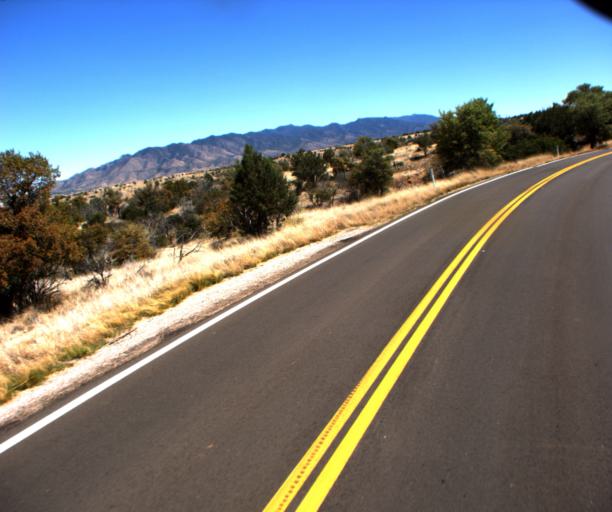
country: US
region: Arizona
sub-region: Cochise County
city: Huachuca City
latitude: 31.5642
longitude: -110.5558
